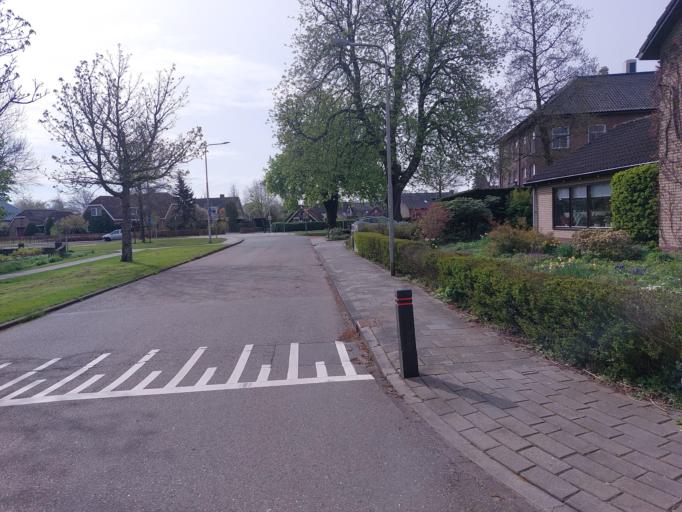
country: NL
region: Gelderland
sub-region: Gemeente Geldermalsen
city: Geldermalsen
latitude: 51.8825
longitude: 5.2780
